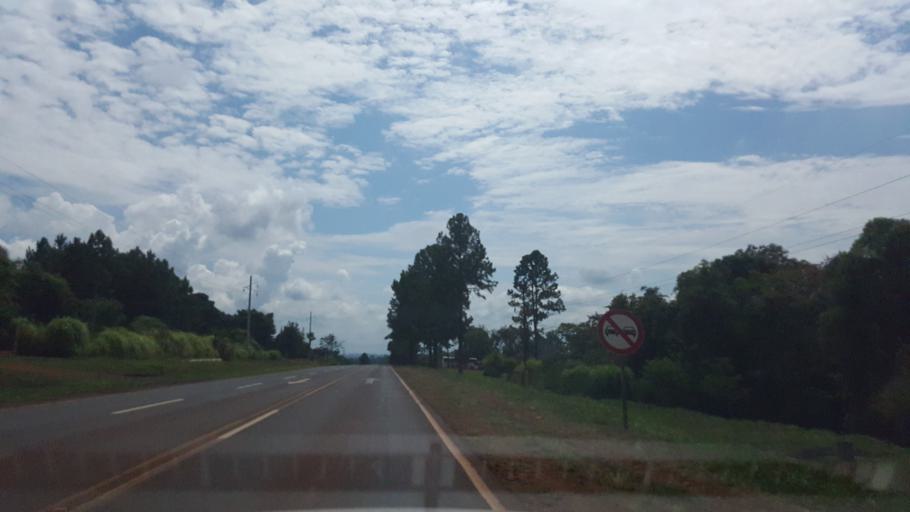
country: AR
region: Misiones
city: Puerto Rico
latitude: -26.8398
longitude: -55.0393
